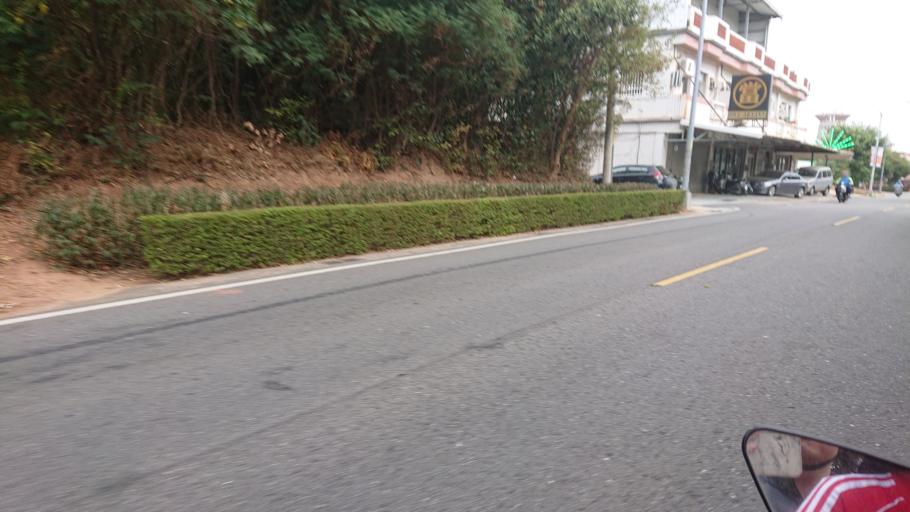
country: TW
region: Fukien
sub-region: Kinmen
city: Jincheng
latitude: 24.4186
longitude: 118.3101
